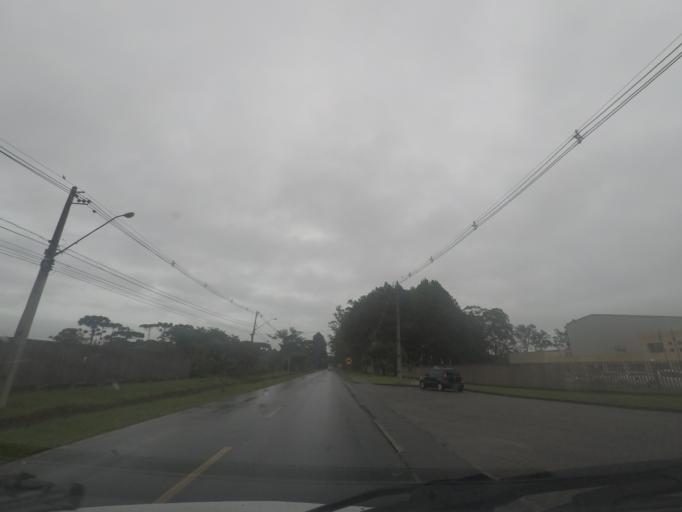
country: BR
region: Parana
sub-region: Quatro Barras
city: Quatro Barras
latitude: -25.3730
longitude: -49.0895
